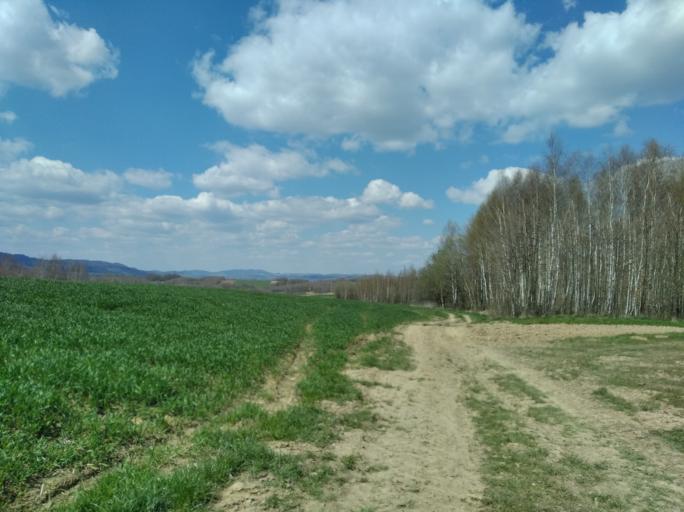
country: PL
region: Subcarpathian Voivodeship
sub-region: Powiat strzyzowski
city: Wysoka Strzyzowska
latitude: 49.8419
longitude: 21.7612
